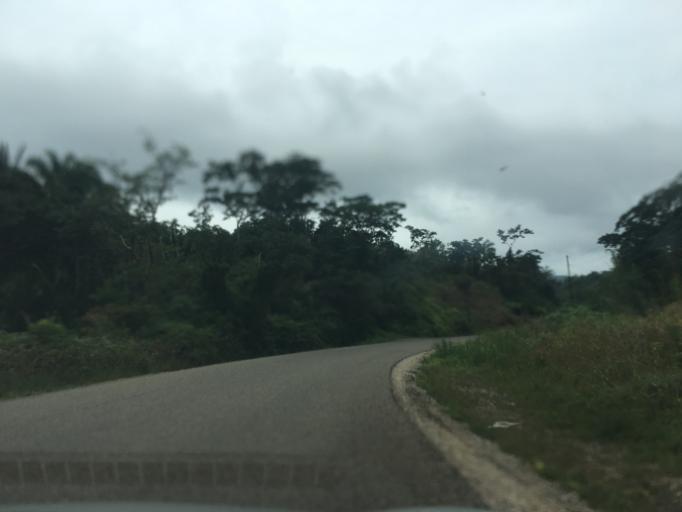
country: BZ
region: Cayo
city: Belmopan
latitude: 17.0489
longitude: -88.5411
